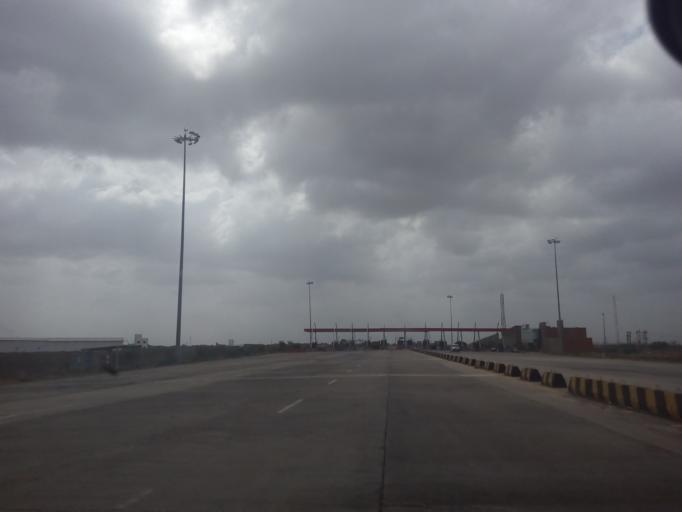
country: IN
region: Gujarat
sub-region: Rajkot
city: Morbi
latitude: 23.0378
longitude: 70.9263
